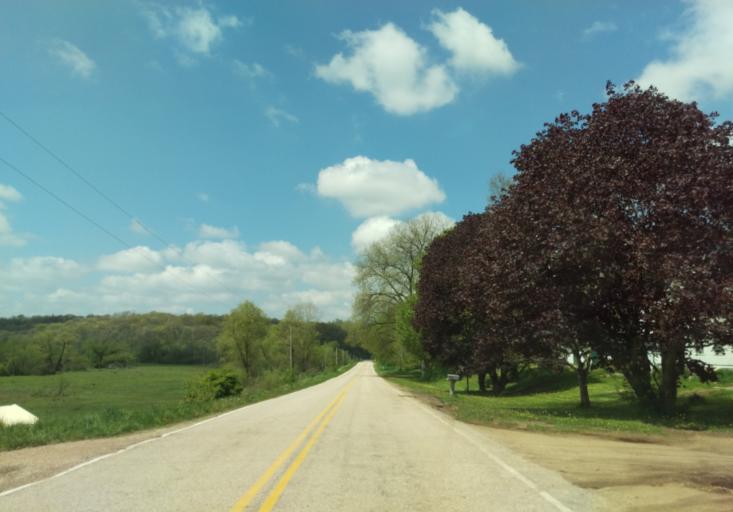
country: US
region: Wisconsin
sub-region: Dane County
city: Mount Horeb
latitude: 43.0585
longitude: -89.7763
